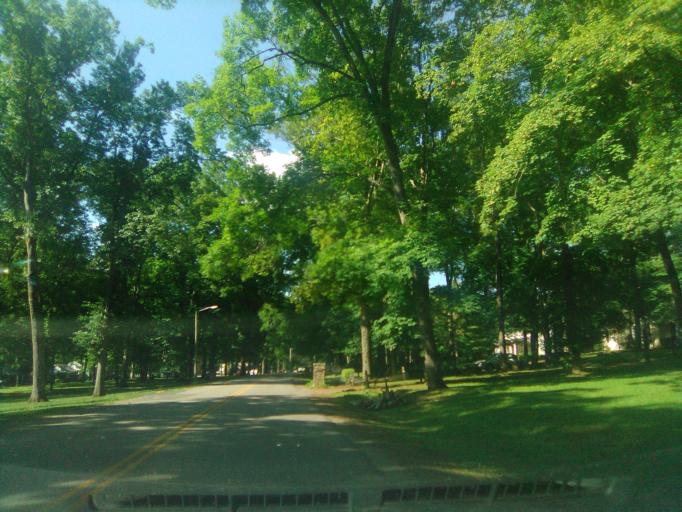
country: US
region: Tennessee
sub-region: Davidson County
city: Belle Meade
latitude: 36.1139
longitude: -86.8714
